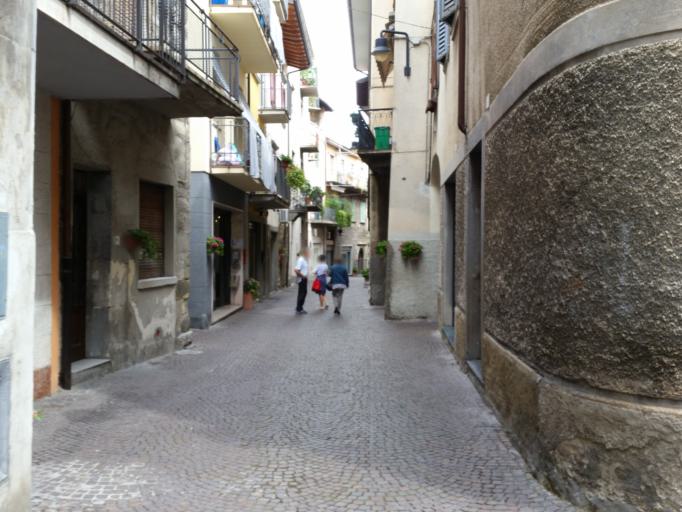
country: IT
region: Lombardy
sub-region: Provincia di Bergamo
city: Sarnico
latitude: 45.6675
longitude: 9.9566
